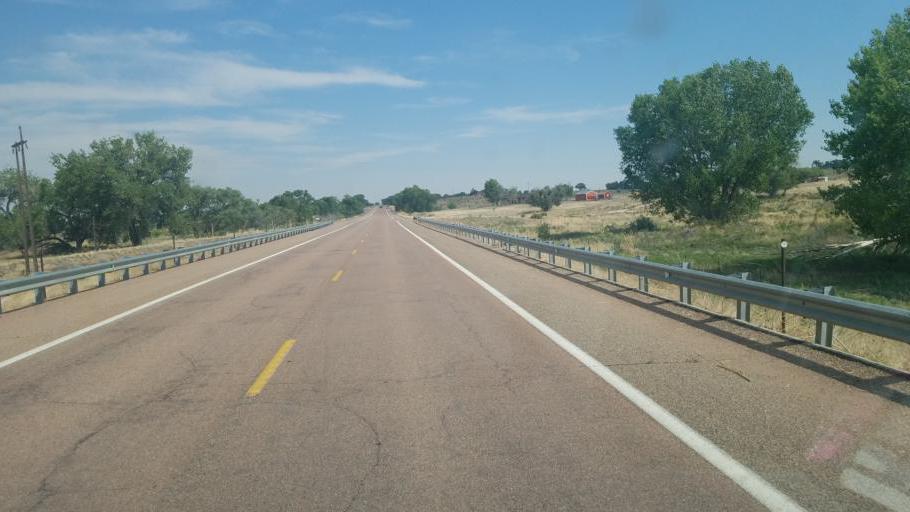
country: US
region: Colorado
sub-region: Pueblo County
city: Pueblo
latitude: 38.2428
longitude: -104.3409
